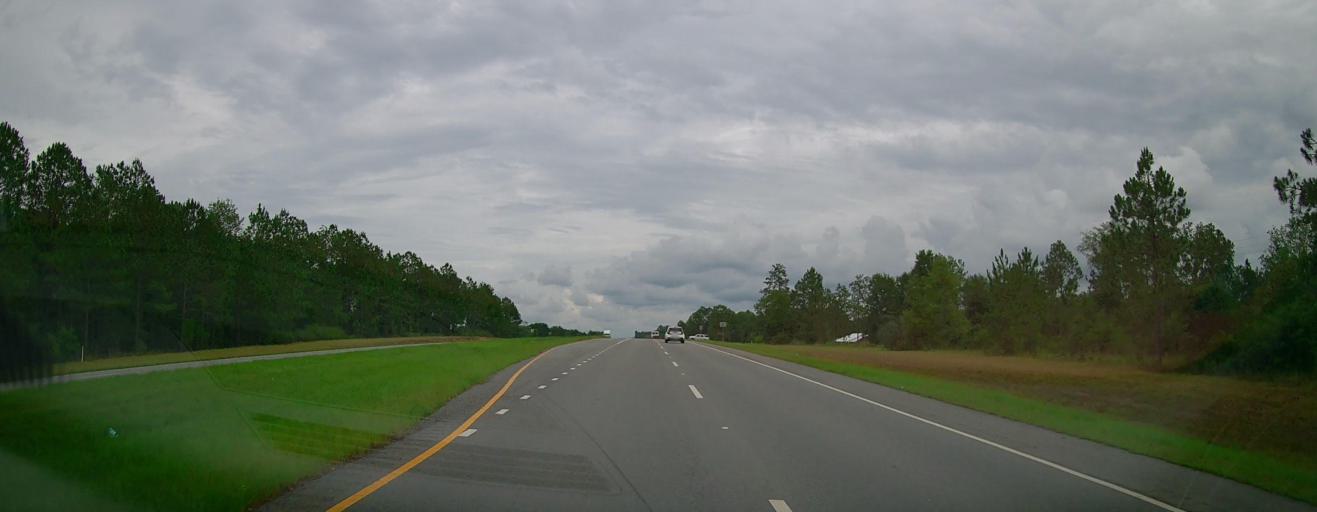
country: US
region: Georgia
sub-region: Telfair County
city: Helena
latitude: 32.0868
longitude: -82.9341
